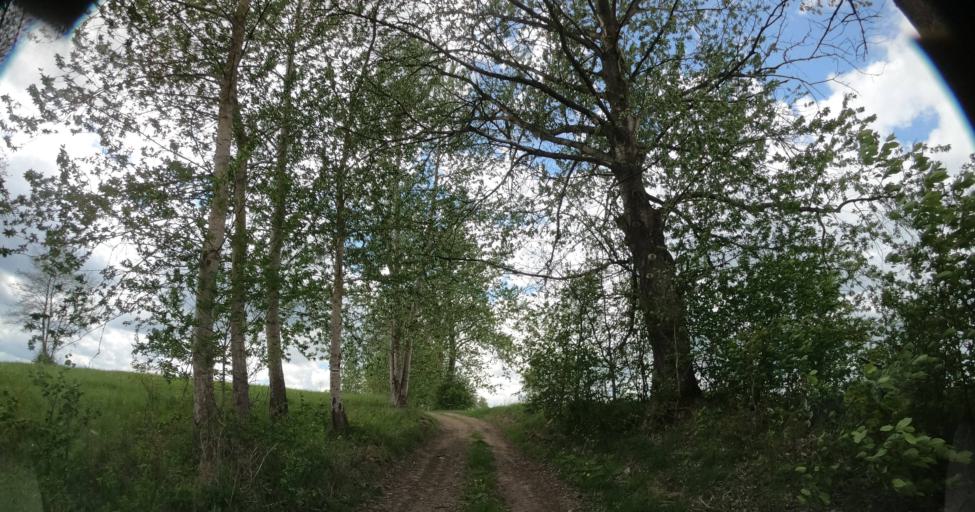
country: PL
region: West Pomeranian Voivodeship
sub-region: Powiat drawski
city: Drawsko Pomorskie
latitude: 53.5623
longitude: 15.7733
